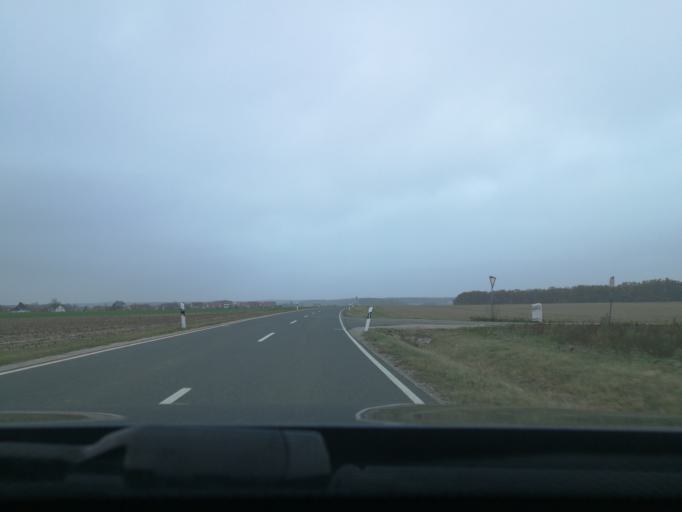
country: DE
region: Bavaria
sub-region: Regierungsbezirk Mittelfranken
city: Puschendorf
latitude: 49.5661
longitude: 10.8334
